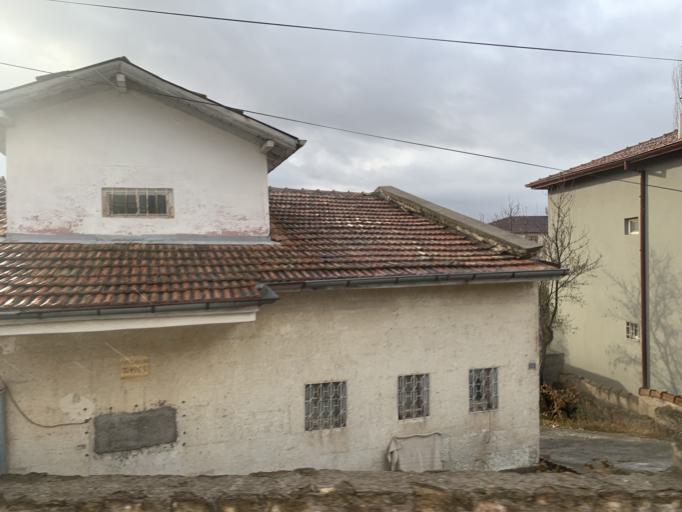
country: TR
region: Nevsehir
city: Avanos
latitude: 38.7206
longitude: 34.8548
